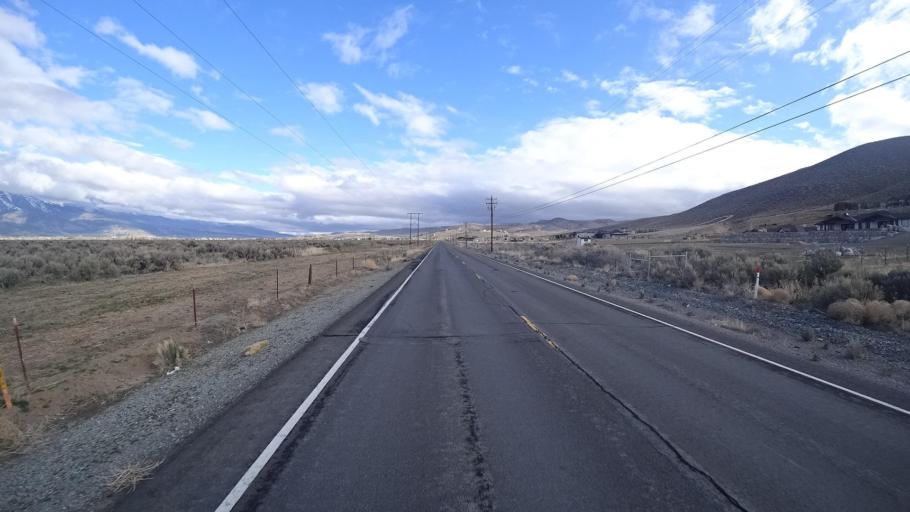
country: US
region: Nevada
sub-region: Carson City
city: Carson City
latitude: 39.2625
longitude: -119.7567
